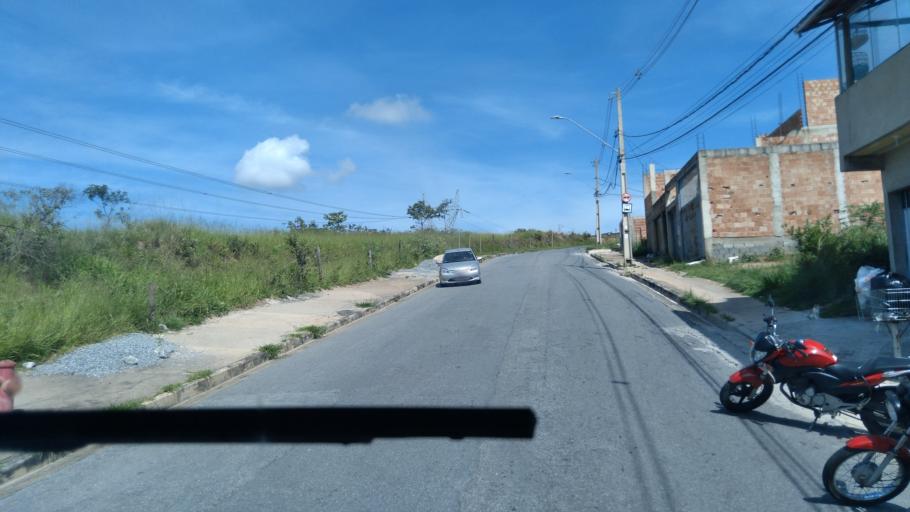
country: BR
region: Minas Gerais
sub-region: Santa Luzia
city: Santa Luzia
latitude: -19.8435
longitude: -43.8798
